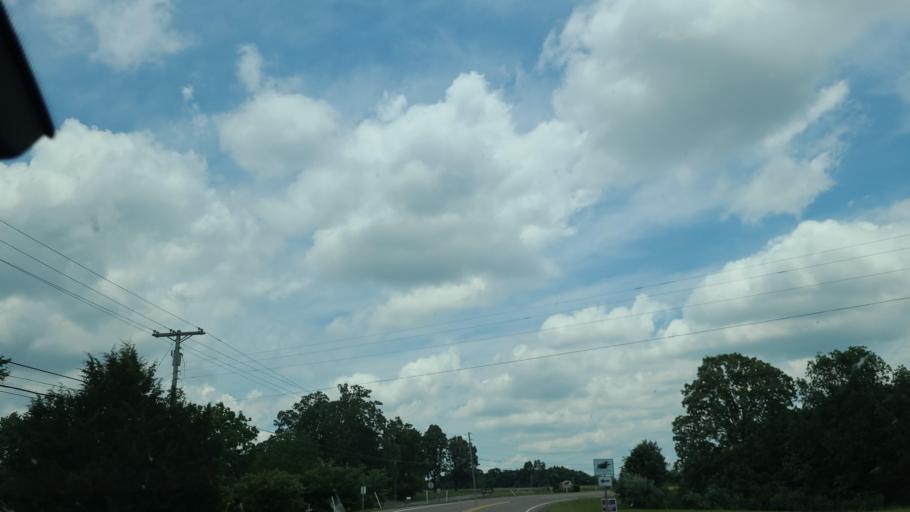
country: US
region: Tennessee
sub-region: Cumberland County
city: Lake Tansi
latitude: 35.8862
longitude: -85.0021
